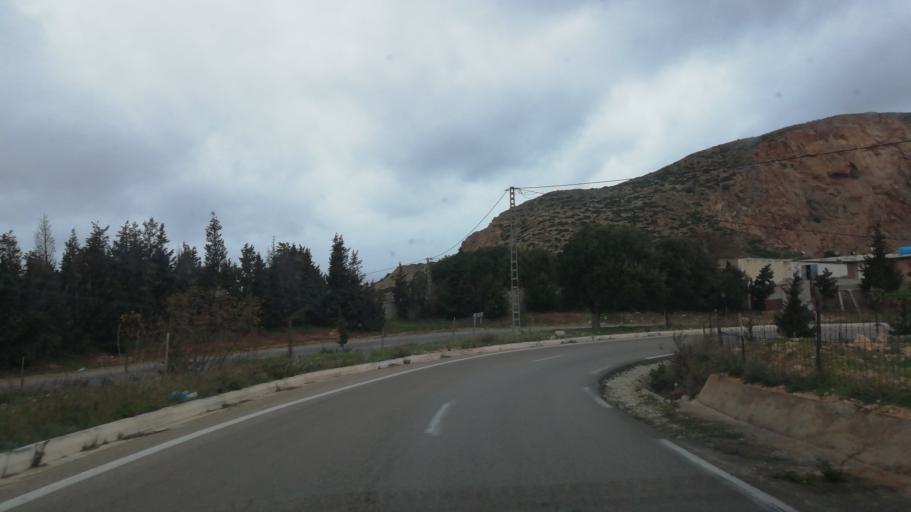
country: DZ
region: Oran
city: Mers el Kebir
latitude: 35.7206
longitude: -0.7355
